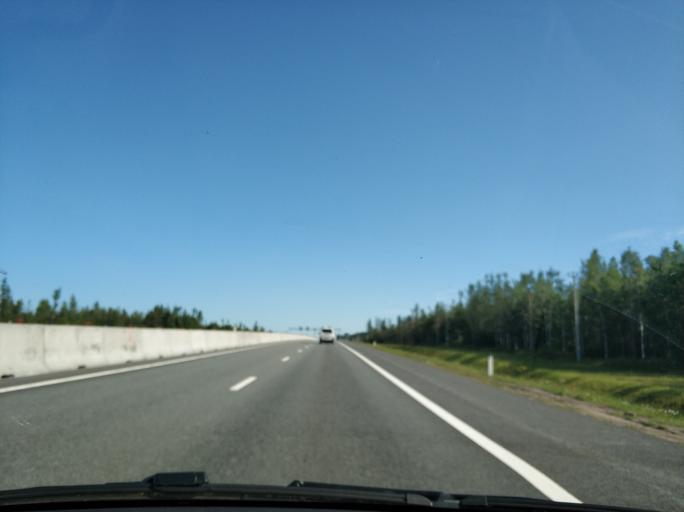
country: RU
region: Leningrad
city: Sosnovo
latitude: 60.4679
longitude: 30.1961
